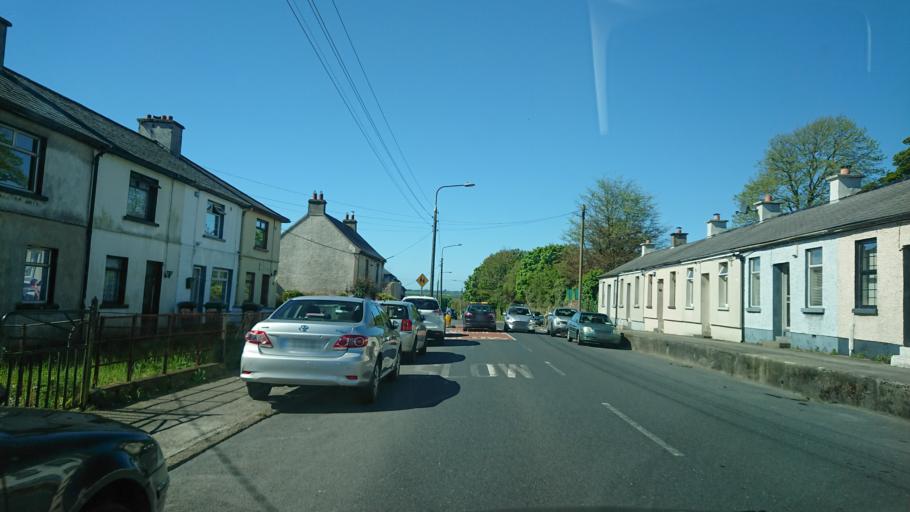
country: IE
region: Munster
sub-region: Waterford
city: Waterford
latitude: 52.2531
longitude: -7.1248
